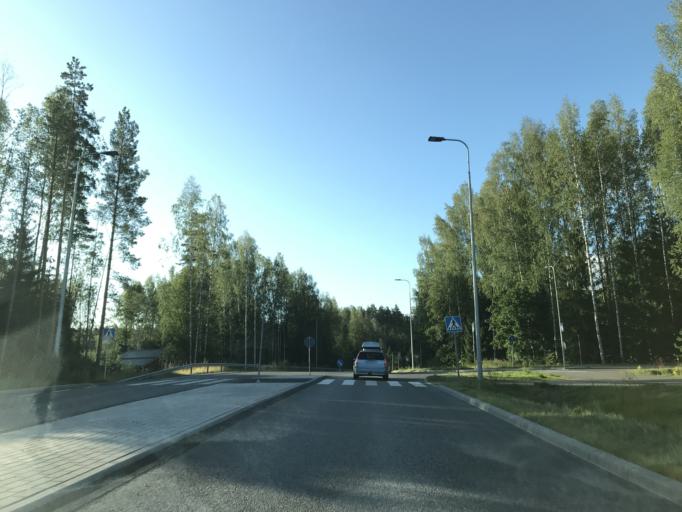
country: FI
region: Uusimaa
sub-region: Helsinki
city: Kauniainen
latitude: 60.3235
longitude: 24.7157
